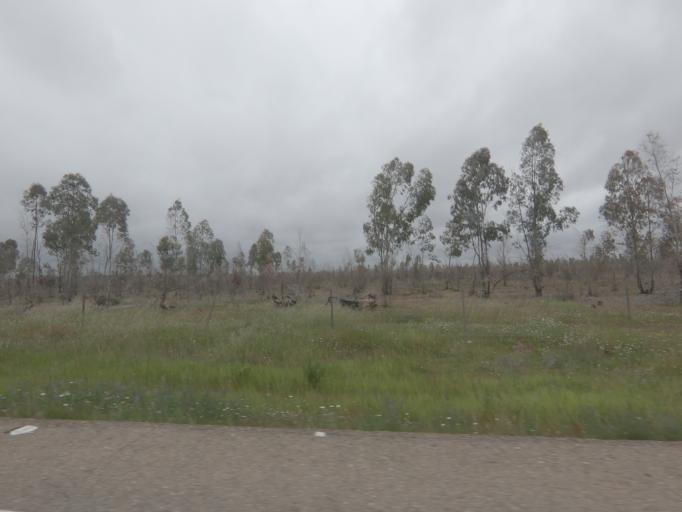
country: ES
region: Extremadura
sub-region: Provincia de Badajoz
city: Badajoz
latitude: 38.9839
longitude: -6.8812
